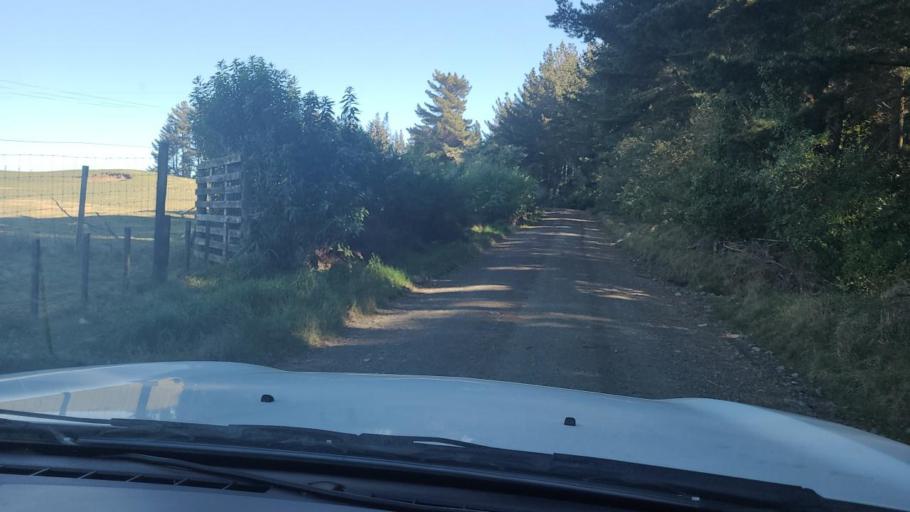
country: NZ
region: Hawke's Bay
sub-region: Napier City
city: Taradale
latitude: -39.4145
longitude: 176.4652
